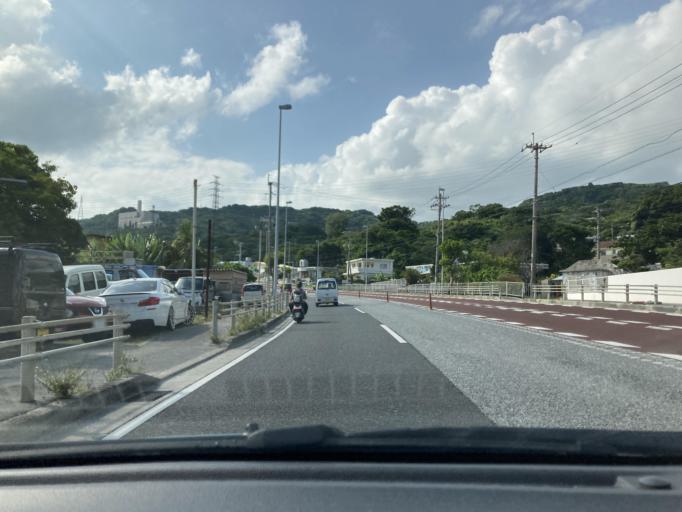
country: JP
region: Okinawa
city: Ginowan
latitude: 26.2778
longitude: 127.8056
